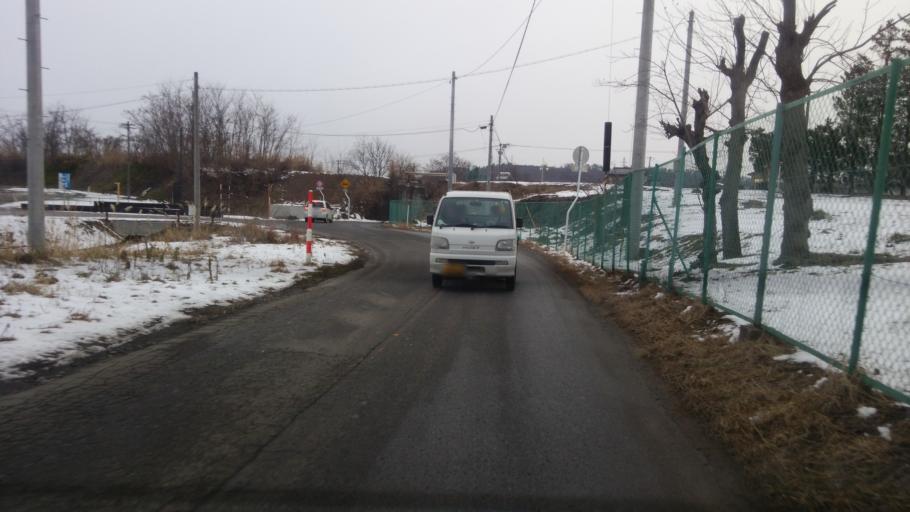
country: JP
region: Fukushima
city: Kitakata
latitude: 37.5657
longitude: 139.9467
